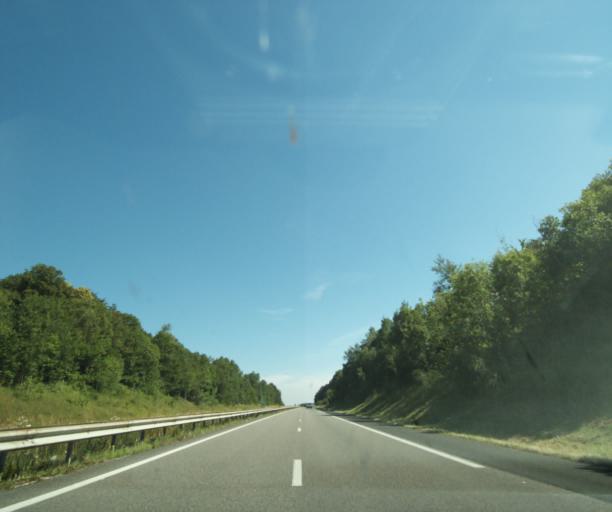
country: FR
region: Lorraine
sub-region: Departement des Vosges
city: Bulgneville
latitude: 48.2455
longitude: 5.8621
